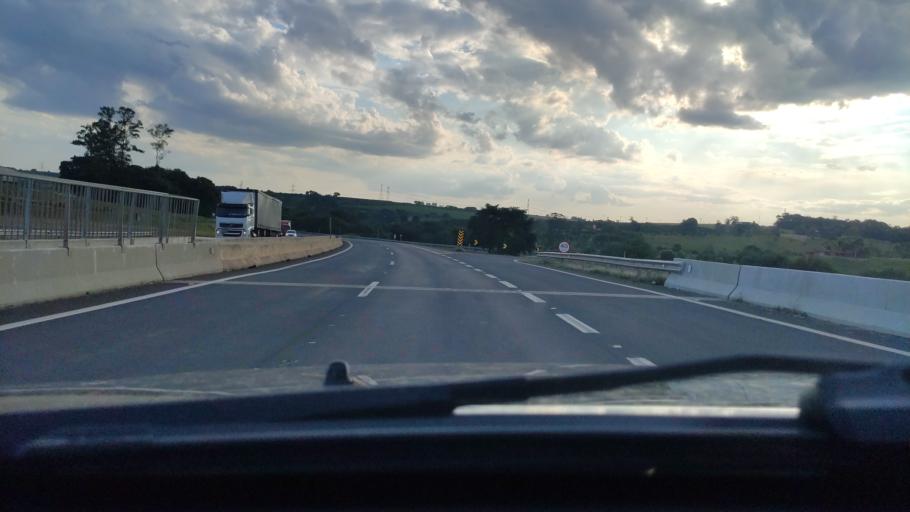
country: BR
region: Sao Paulo
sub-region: Mogi-Mirim
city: Mogi Mirim
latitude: -22.4418
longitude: -47.0496
